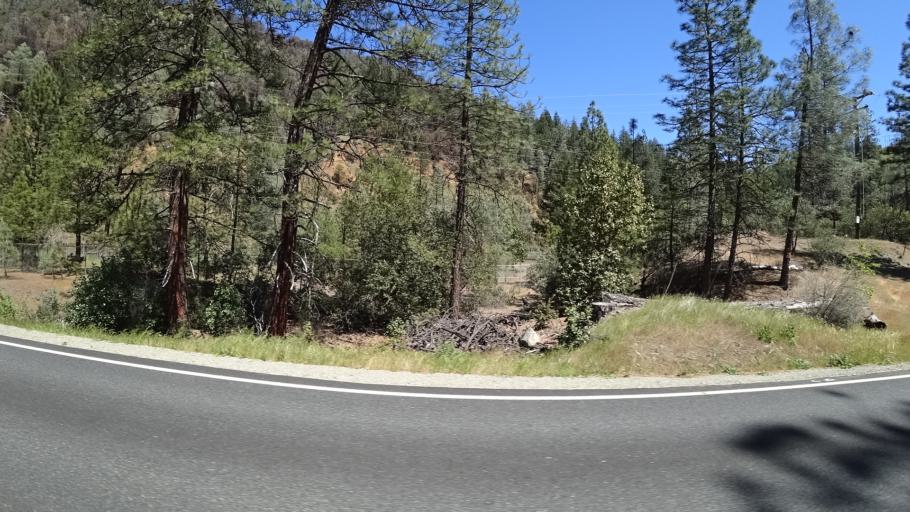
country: US
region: California
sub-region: Trinity County
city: Weaverville
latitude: 40.7574
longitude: -123.0665
